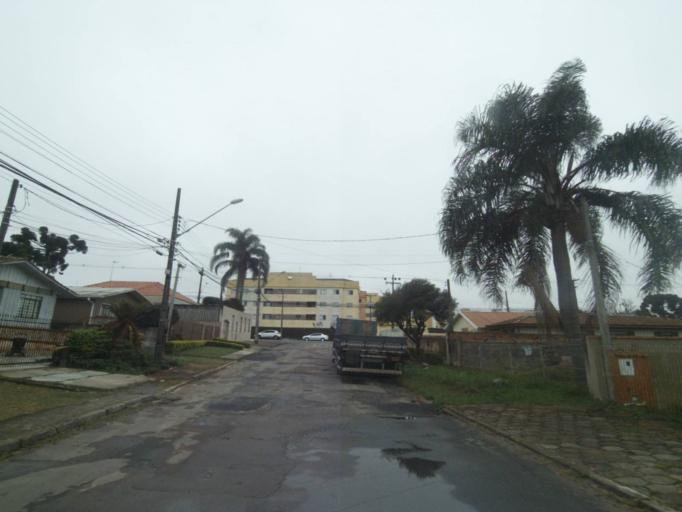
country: BR
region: Parana
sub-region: Curitiba
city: Curitiba
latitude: -25.5021
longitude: -49.3028
